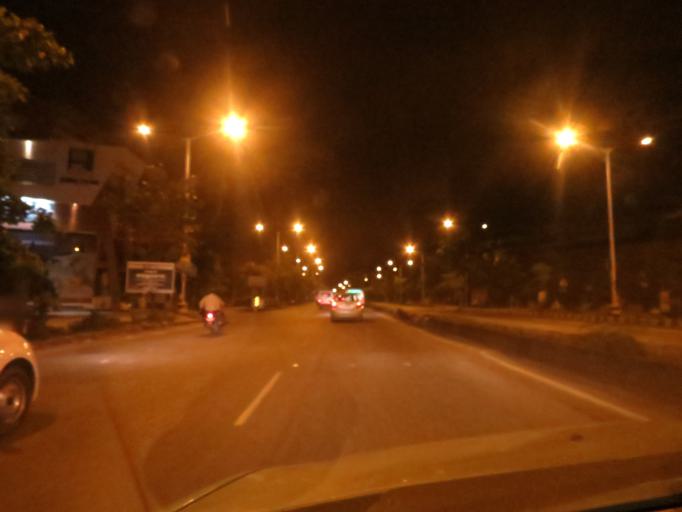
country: IN
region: Karnataka
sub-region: Bangalore Urban
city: Bangalore
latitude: 13.0034
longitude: 77.6632
